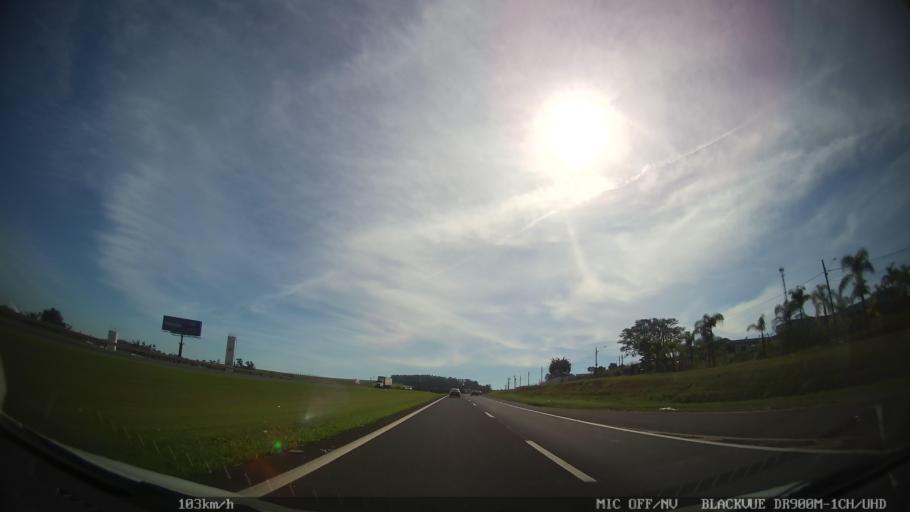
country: BR
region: Sao Paulo
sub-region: Araras
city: Araras
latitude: -22.3475
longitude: -47.3941
